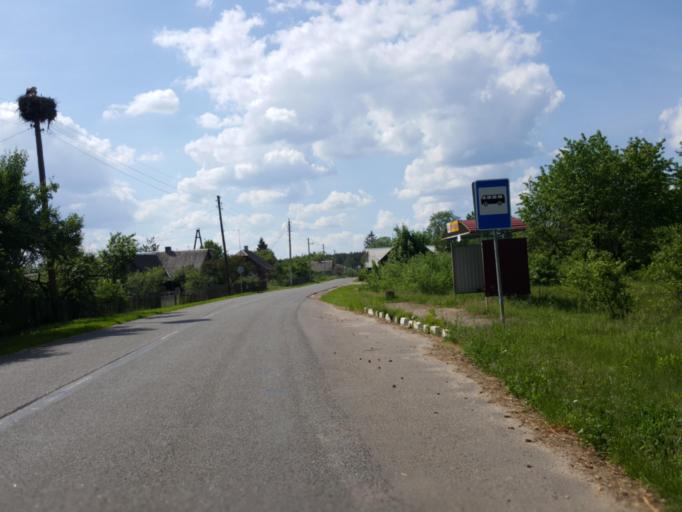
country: BY
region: Brest
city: Kamyanyuki
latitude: 52.5042
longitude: 23.6578
